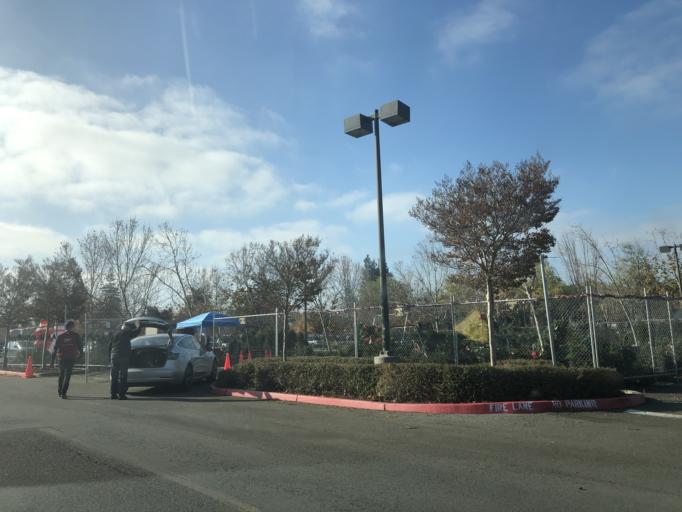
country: US
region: California
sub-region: Santa Clara County
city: Sunnyvale
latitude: 37.3832
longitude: -122.0111
